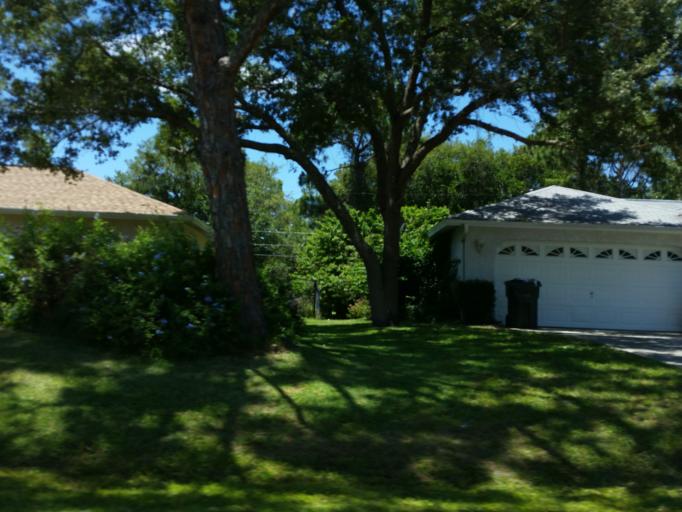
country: US
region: Florida
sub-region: Sarasota County
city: North Port
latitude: 27.0594
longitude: -82.1974
